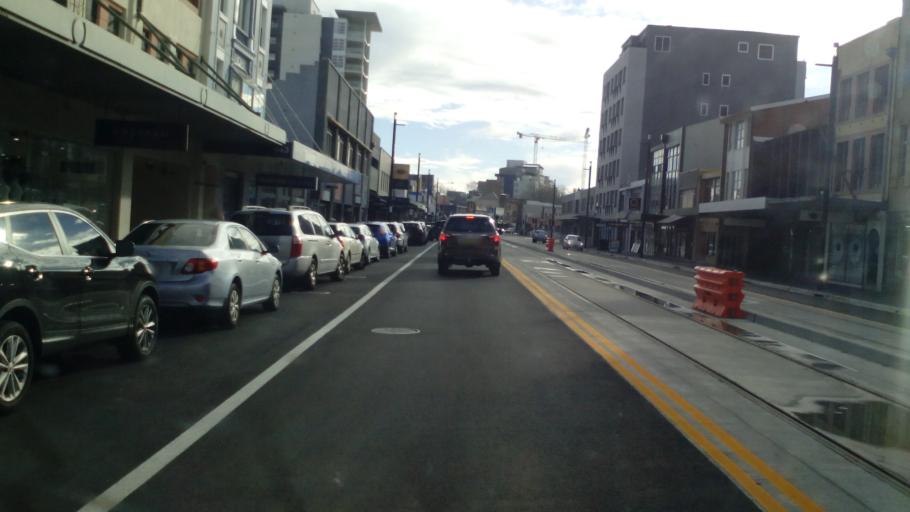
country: AU
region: New South Wales
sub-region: Newcastle
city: Cooks Hill
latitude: -32.9273
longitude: 151.7706
